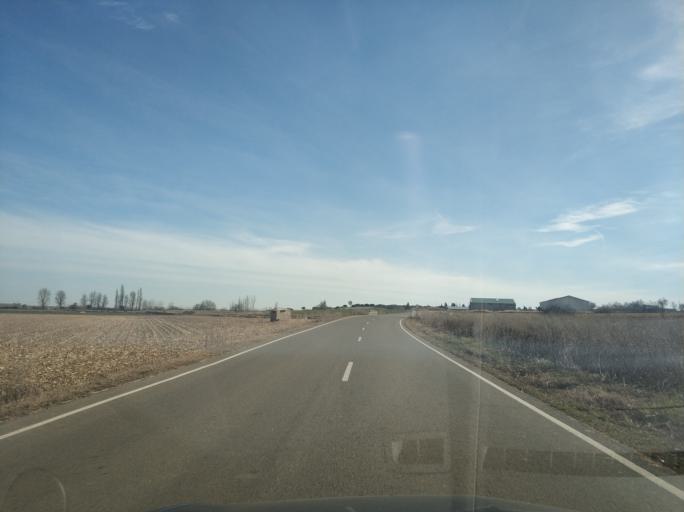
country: ES
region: Castille and Leon
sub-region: Provincia de Salamanca
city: Florida de Liebana
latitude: 41.0314
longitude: -5.7655
